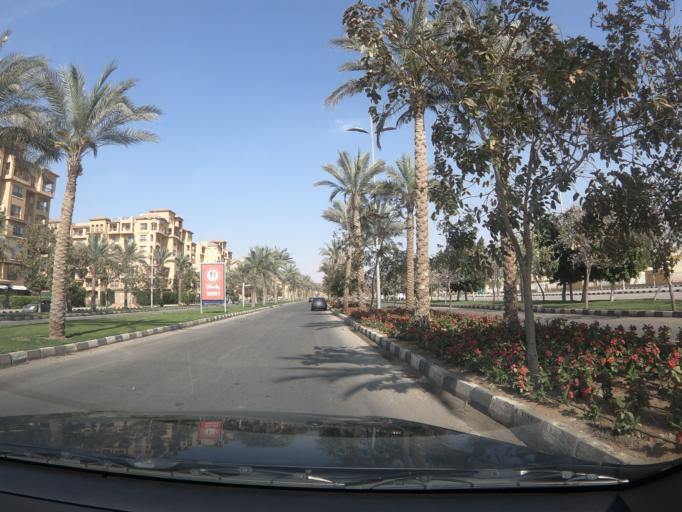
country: EG
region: Muhafazat al Qalyubiyah
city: Al Khankah
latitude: 30.0962
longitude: 31.6375
